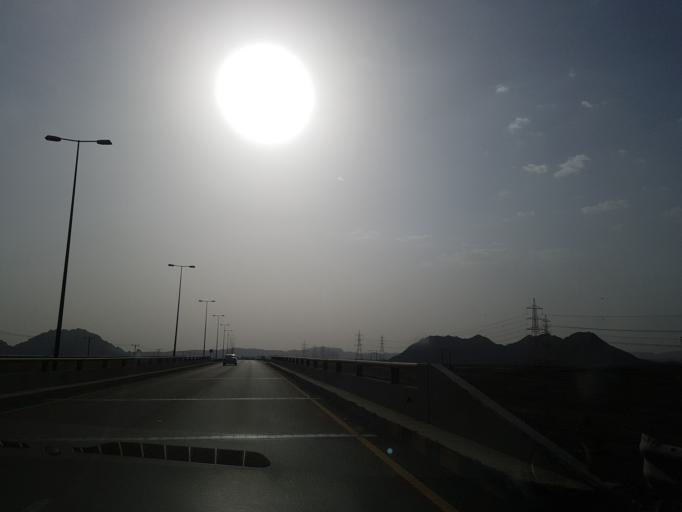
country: OM
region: Al Buraimi
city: Al Buraymi
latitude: 24.2469
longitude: 56.0136
